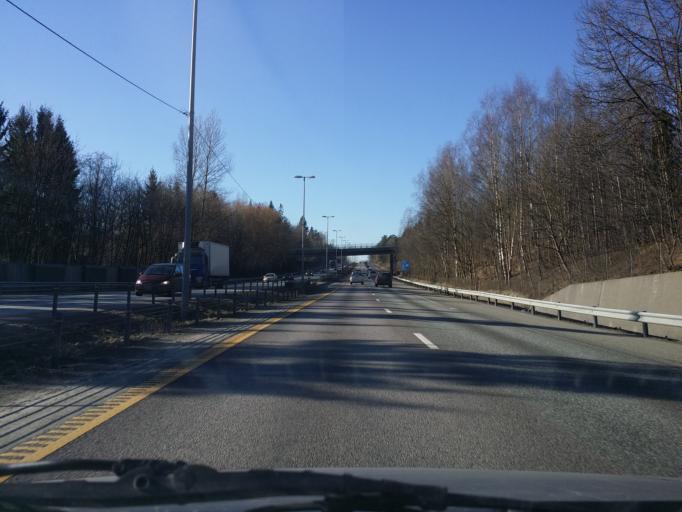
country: NO
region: Akershus
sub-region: Asker
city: Billingstad
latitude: 59.8478
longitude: 10.4748
